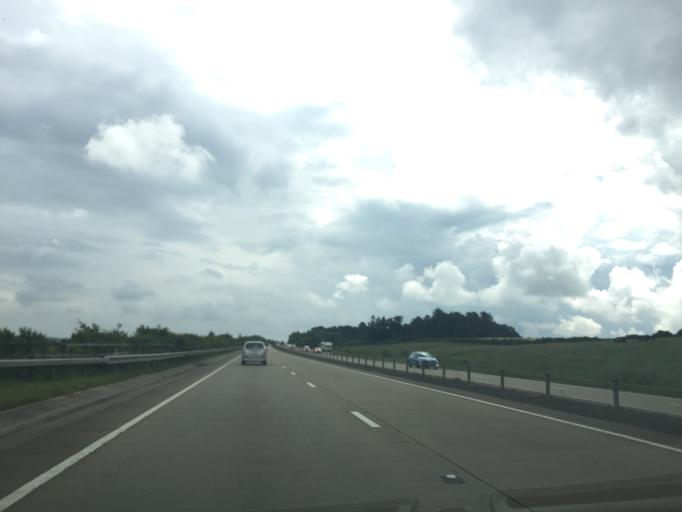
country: GB
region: England
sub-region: Dorset
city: Bovington Camp
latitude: 50.7537
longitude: -2.2807
